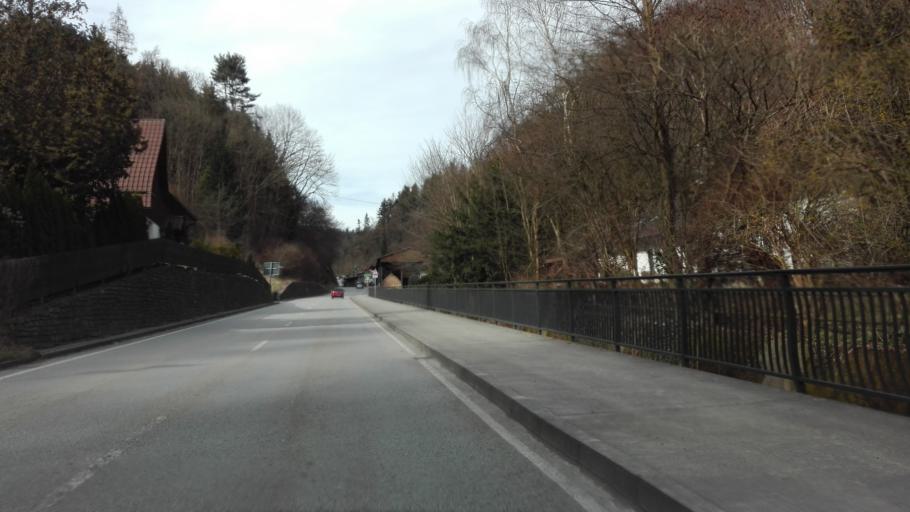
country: DE
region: Bavaria
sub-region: Lower Bavaria
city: Thyrnau
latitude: 48.5927
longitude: 13.5132
